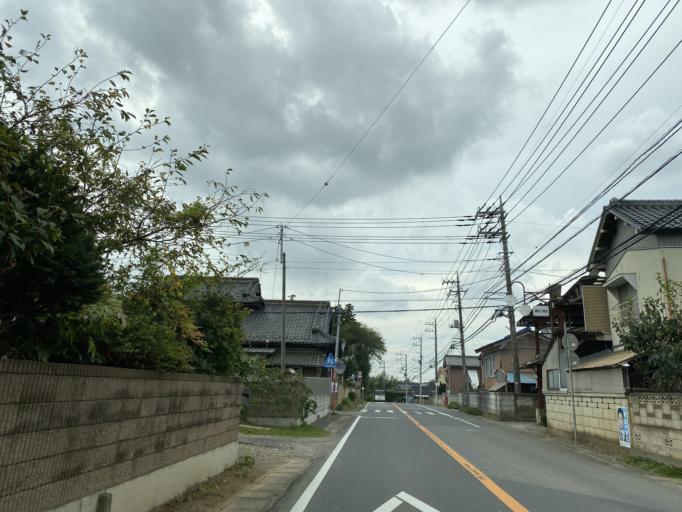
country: JP
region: Ibaraki
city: Mitsukaido
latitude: 35.9886
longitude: 140.0437
